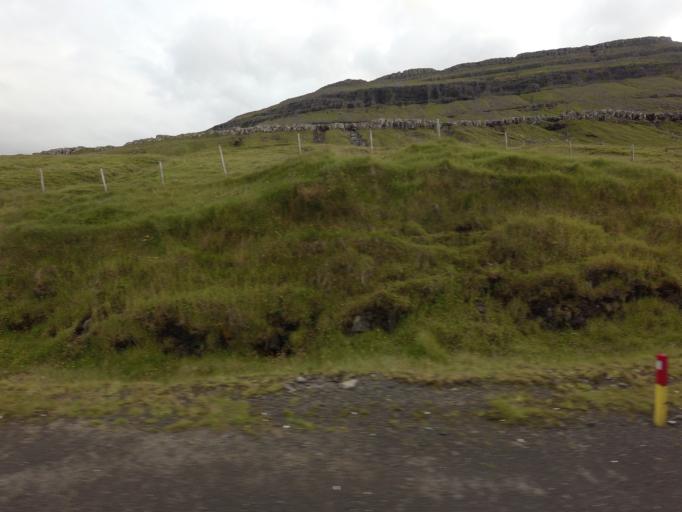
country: FO
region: Streymoy
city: Kollafjordhur
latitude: 62.1405
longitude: -6.8957
